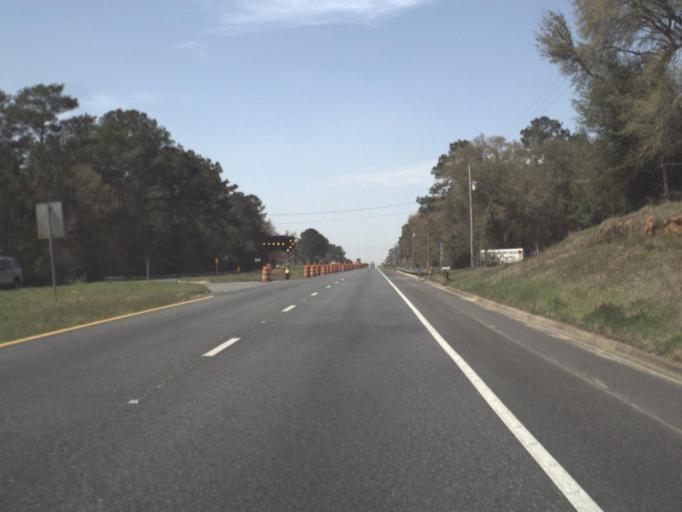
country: US
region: Florida
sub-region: Gadsden County
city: Quincy
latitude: 30.5662
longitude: -84.5437
